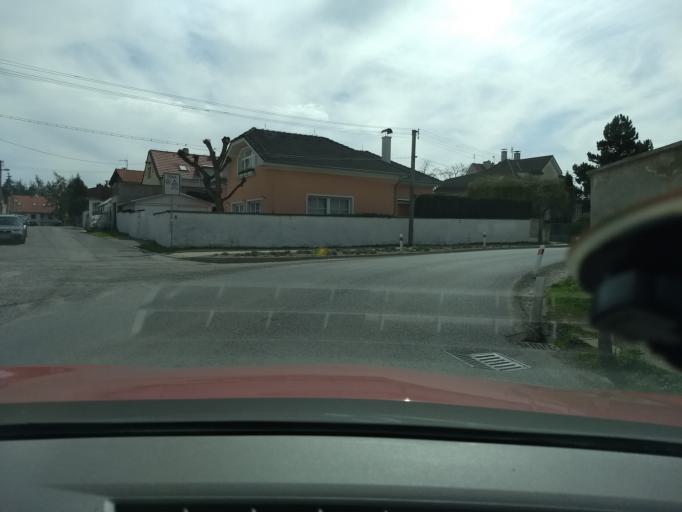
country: CZ
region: Central Bohemia
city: Rudna
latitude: 50.0604
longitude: 14.2275
